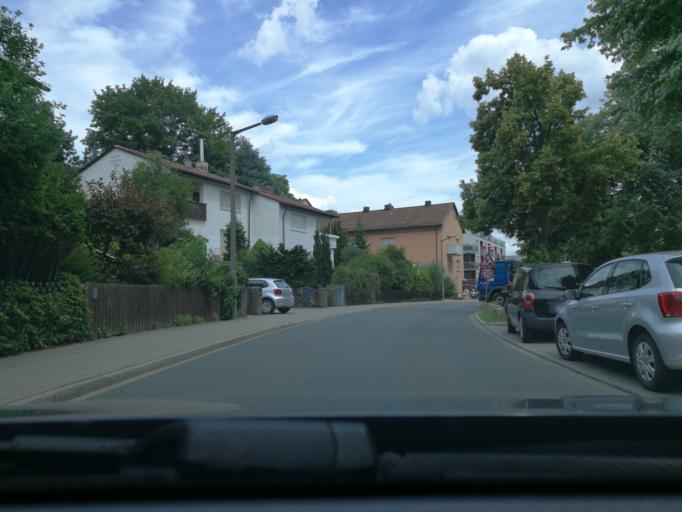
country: DE
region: Bavaria
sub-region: Regierungsbezirk Mittelfranken
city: Furth
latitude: 49.4756
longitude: 10.9747
